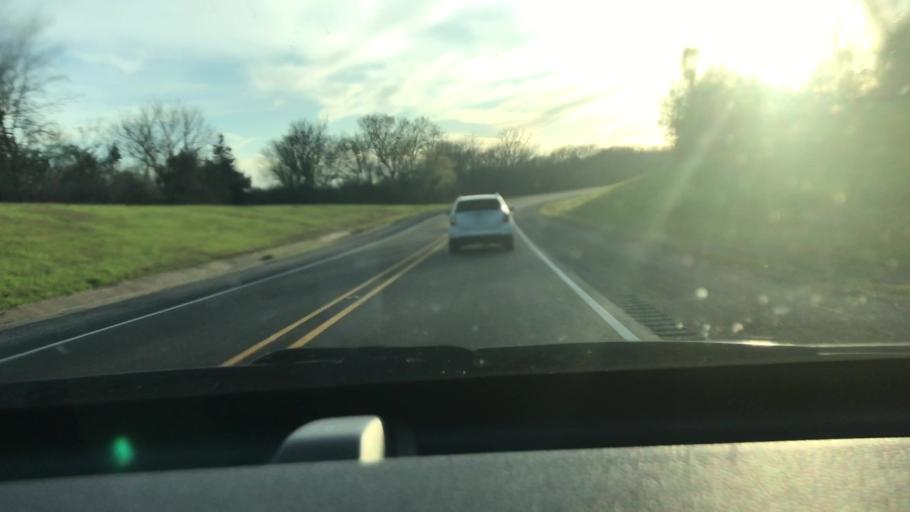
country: US
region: Texas
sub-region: Red River County
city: Clarksville
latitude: 33.5873
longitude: -94.9348
